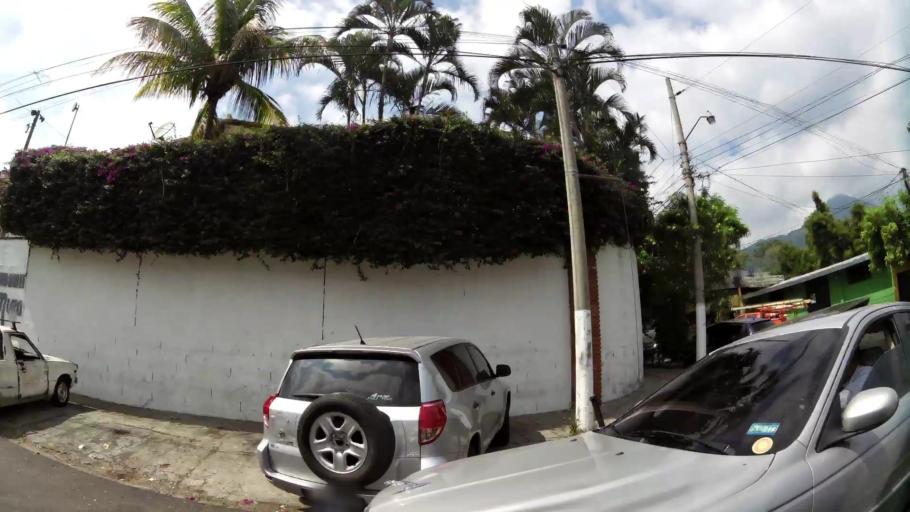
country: SV
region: San Salvador
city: Mejicanos
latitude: 13.7100
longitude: -89.2429
